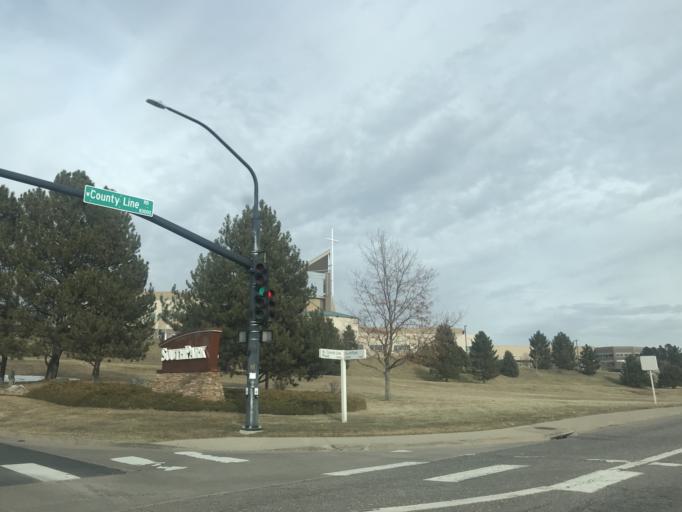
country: US
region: Colorado
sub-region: Douglas County
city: Highlands Ranch
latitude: 39.5655
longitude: -104.9960
